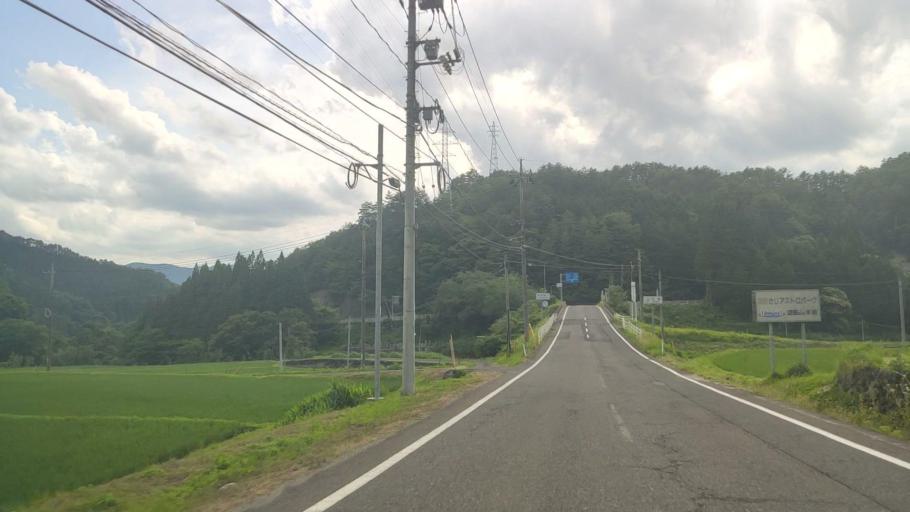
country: JP
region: Tottori
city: Kurayoshi
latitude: 35.2923
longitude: 133.9479
